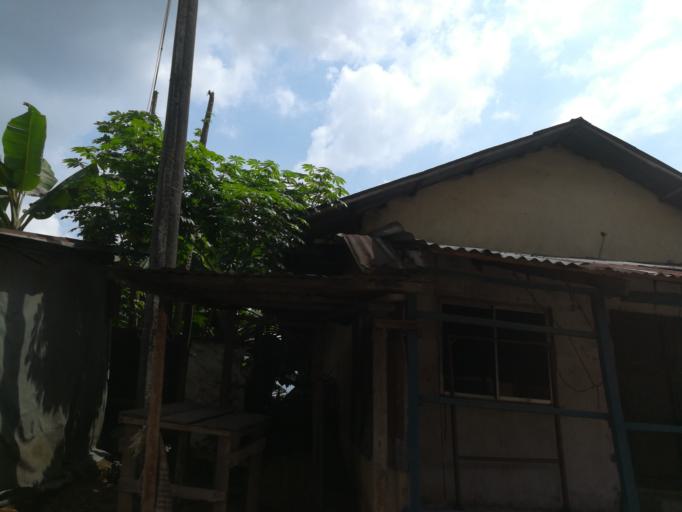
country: NG
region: Rivers
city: Okrika
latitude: 4.7340
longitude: 7.1532
